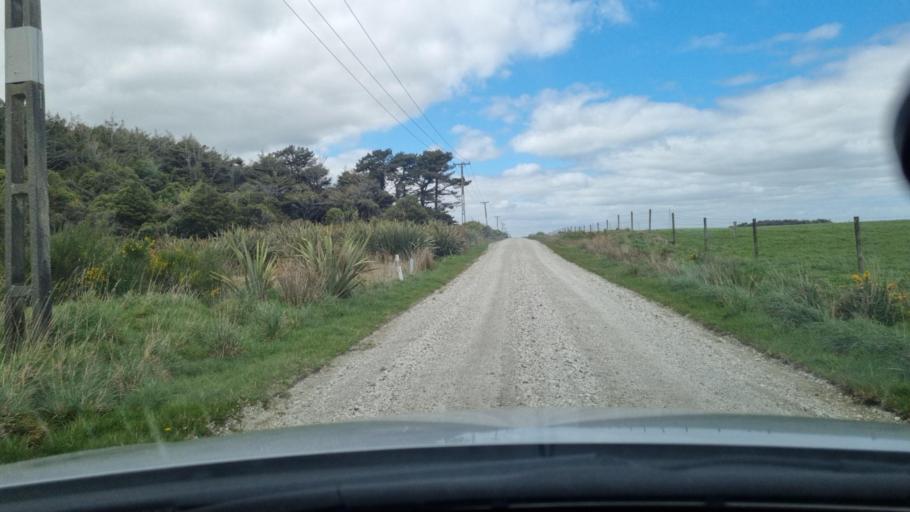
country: NZ
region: Southland
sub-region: Invercargill City
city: Invercargill
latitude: -46.4427
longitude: 168.4260
